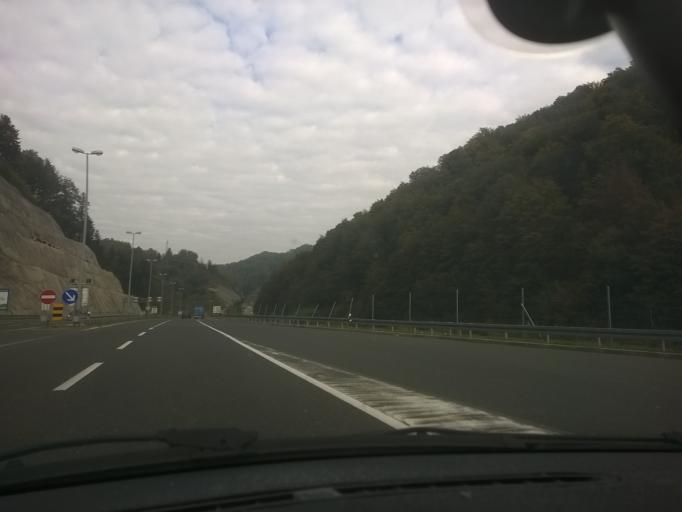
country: SI
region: Zetale
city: Zetale
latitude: 46.2684
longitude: 15.8685
